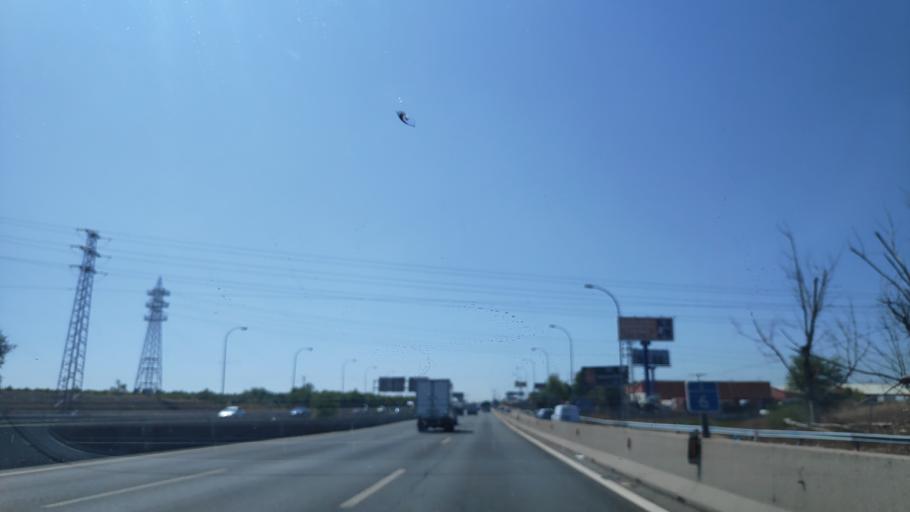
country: ES
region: Madrid
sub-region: Provincia de Madrid
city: Villaverde
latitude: 40.3624
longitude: -3.7212
